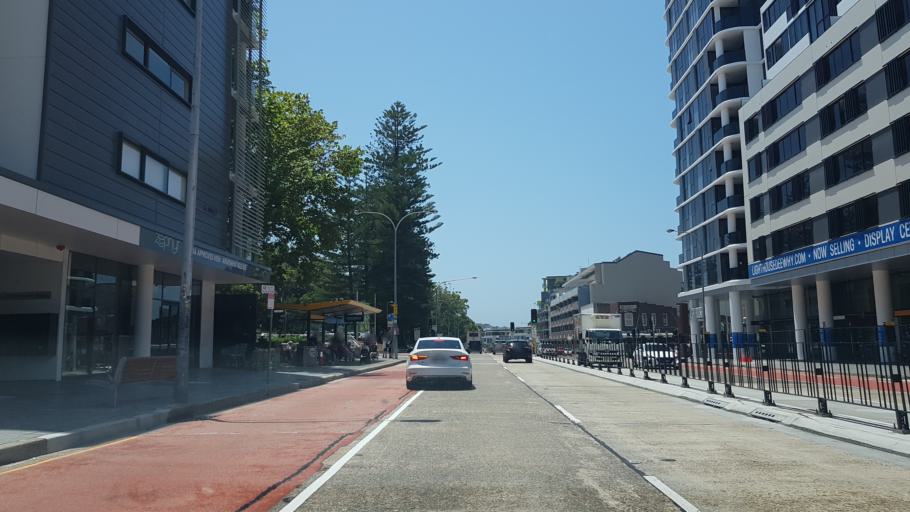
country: AU
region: New South Wales
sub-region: Warringah
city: Narraweena
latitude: -33.7530
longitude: 151.2861
